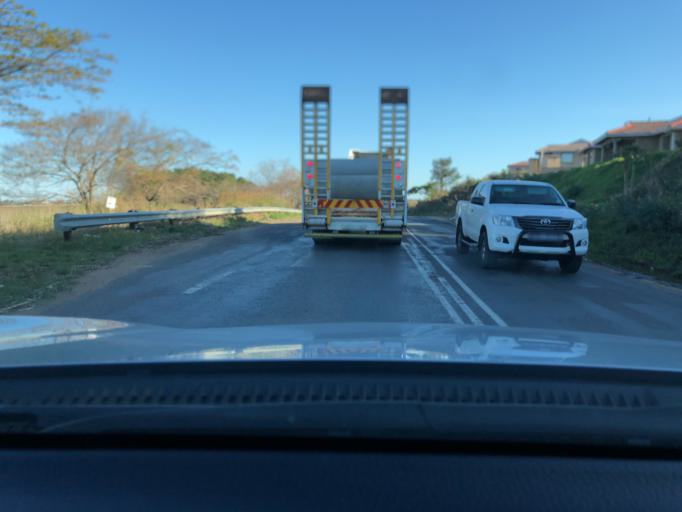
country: ZA
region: KwaZulu-Natal
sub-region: eThekwini Metropolitan Municipality
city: Umkomaas
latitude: -30.0293
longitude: 30.8120
